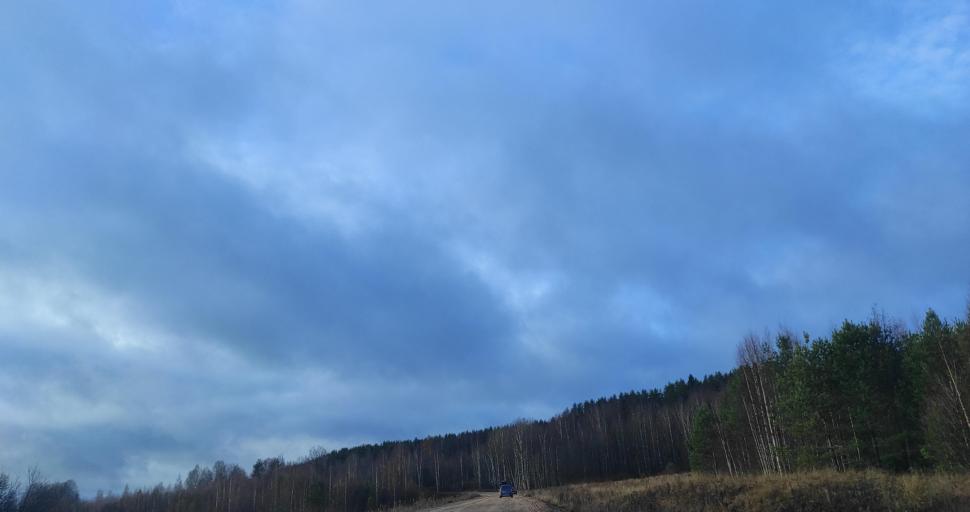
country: RU
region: Republic of Karelia
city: Pitkyaranta
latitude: 61.7133
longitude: 31.3366
